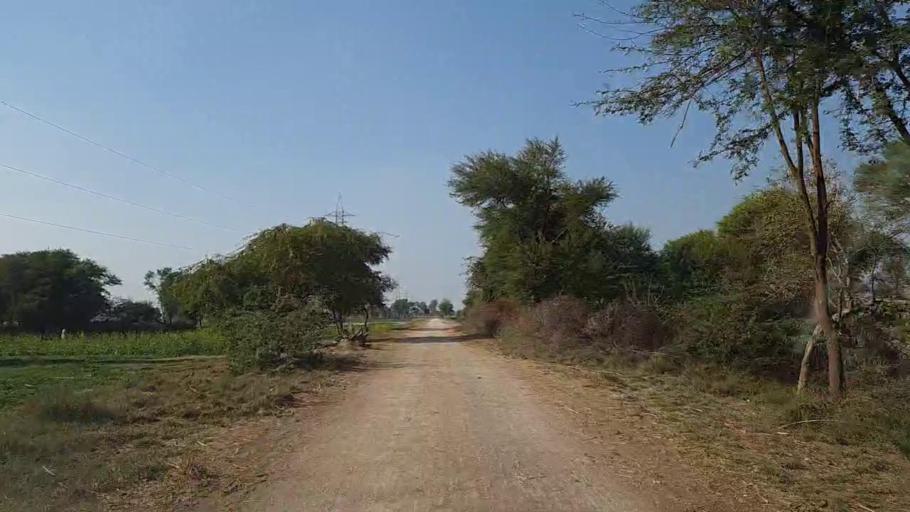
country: PK
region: Sindh
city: Daur
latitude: 26.3825
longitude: 68.3286
